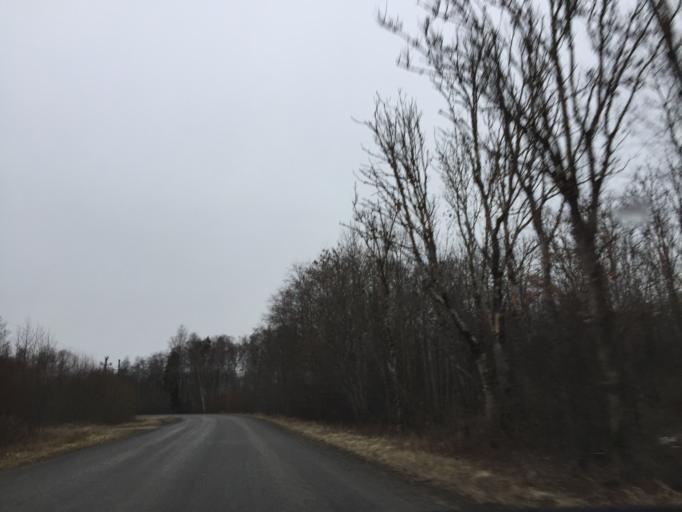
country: EE
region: Laeaene
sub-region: Lihula vald
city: Lihula
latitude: 58.6275
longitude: 23.6331
